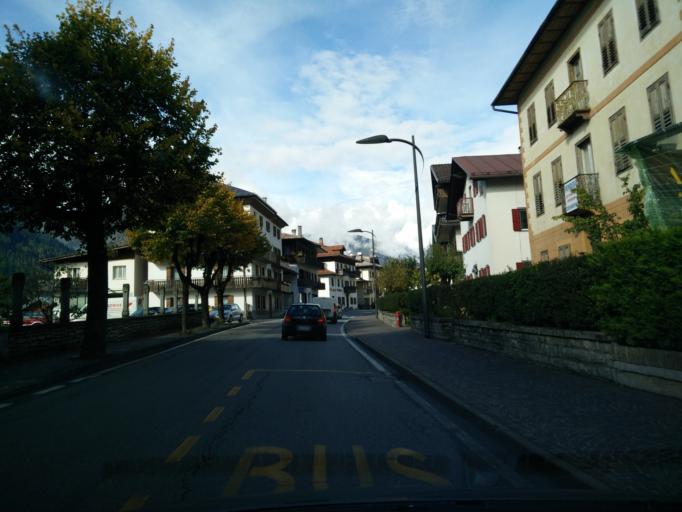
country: IT
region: Veneto
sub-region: Provincia di Belluno
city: Auronzo
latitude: 46.5481
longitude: 12.4511
